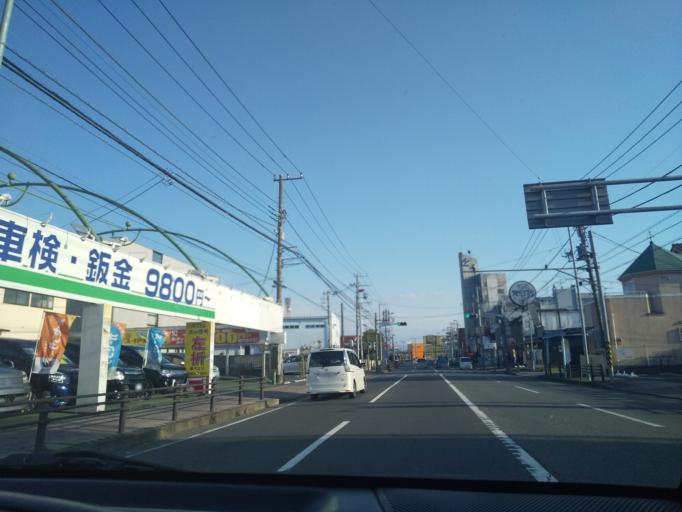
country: JP
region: Kanagawa
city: Zama
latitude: 35.5571
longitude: 139.3751
